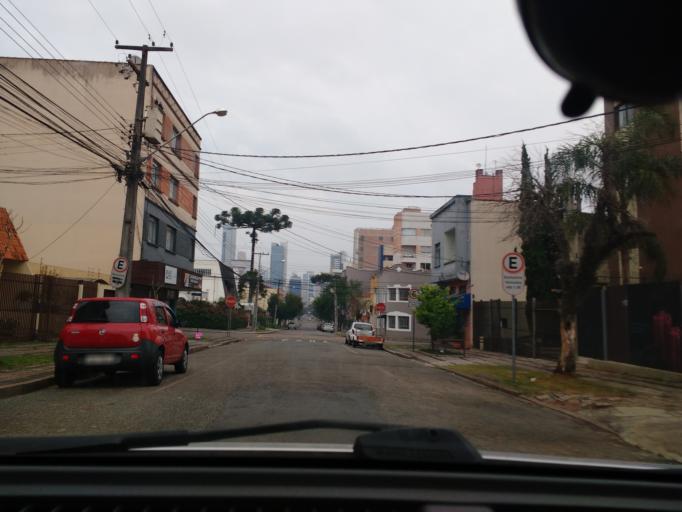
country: BR
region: Parana
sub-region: Curitiba
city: Curitiba
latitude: -25.4275
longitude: -49.2837
